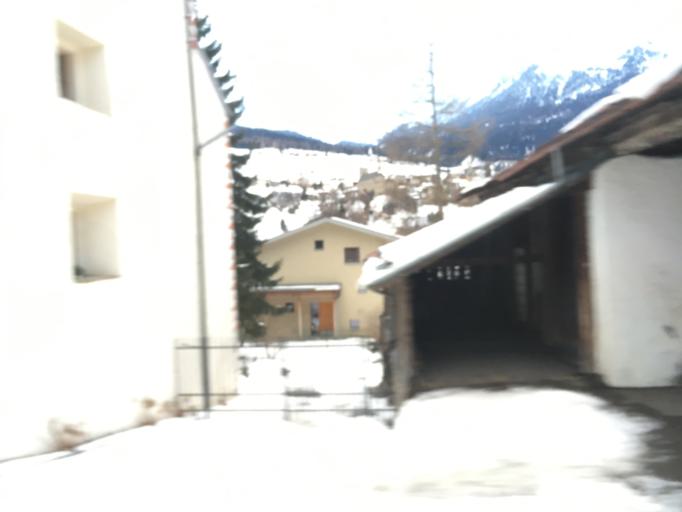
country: CH
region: Grisons
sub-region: Albula District
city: Tiefencastel
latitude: 46.6096
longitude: 9.5917
